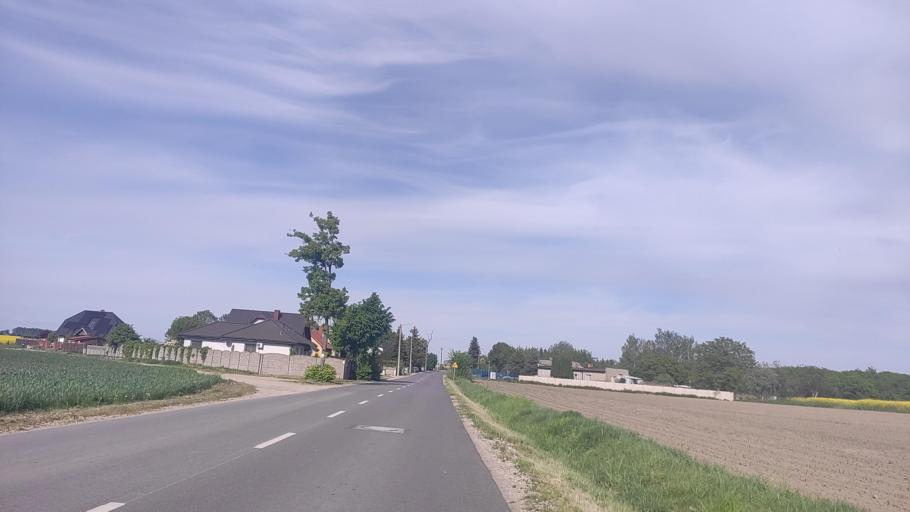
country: PL
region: Greater Poland Voivodeship
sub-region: Powiat poznanski
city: Swarzedz
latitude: 52.4174
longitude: 17.1297
